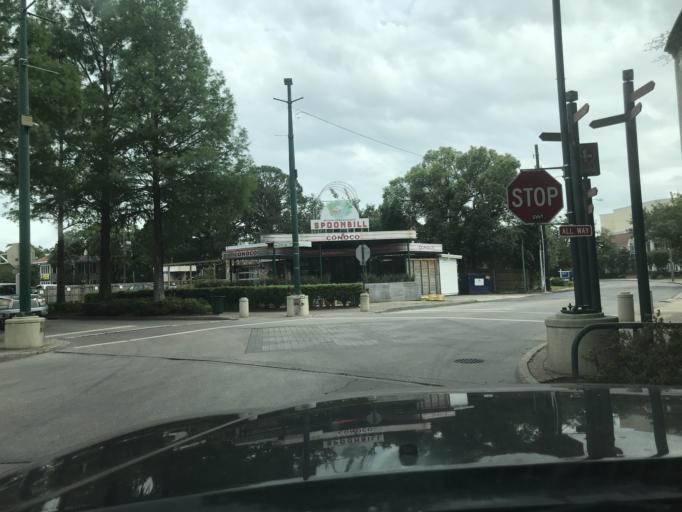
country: US
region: Louisiana
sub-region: Lafayette Parish
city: Lafayette
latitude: 30.2214
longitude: -92.0188
